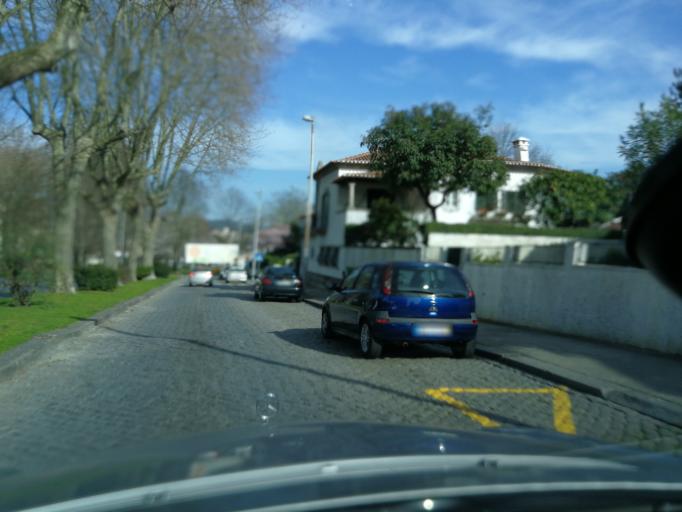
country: PT
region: Braga
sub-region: Vila Nova de Famalicao
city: Calendario
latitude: 41.4063
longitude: -8.5263
